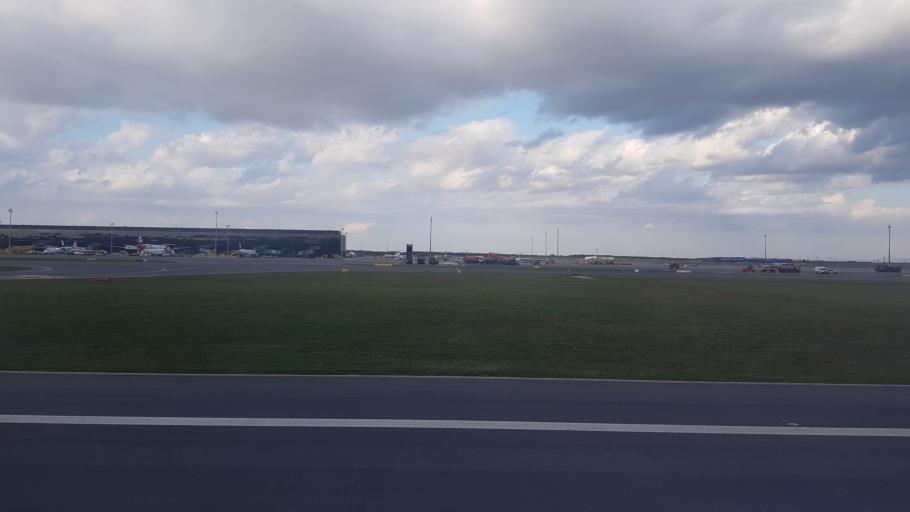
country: AT
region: Lower Austria
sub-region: Politischer Bezirk Bruck an der Leitha
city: Enzersdorf an der Fischa
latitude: 48.1114
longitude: 16.5682
